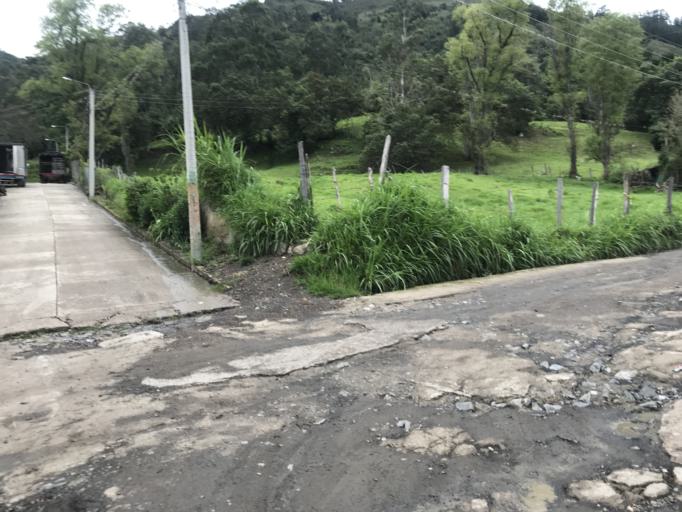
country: CO
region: Boyaca
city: Boavita
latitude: 6.3309
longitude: -72.5836
